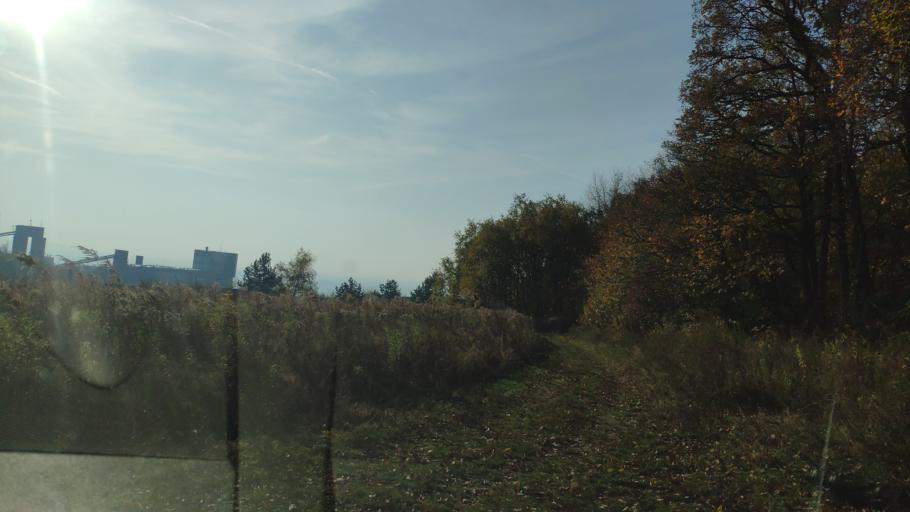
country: SK
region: Kosicky
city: Kosice
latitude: 48.7463
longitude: 21.2198
